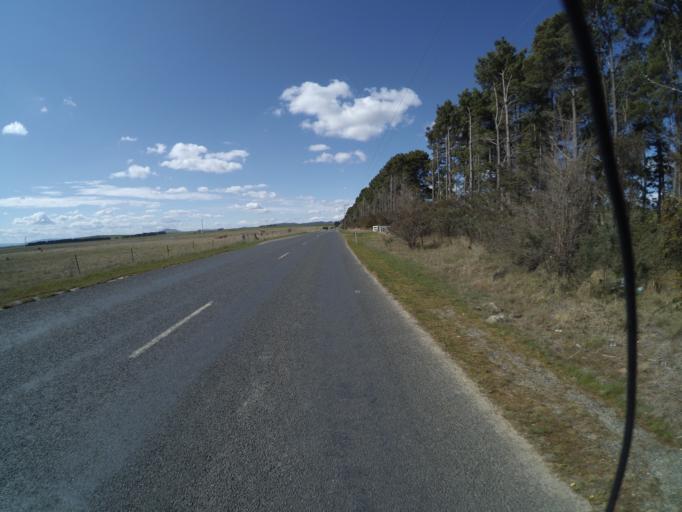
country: AU
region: New South Wales
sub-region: Palerang
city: Bungendore
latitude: -35.2276
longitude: 149.4516
